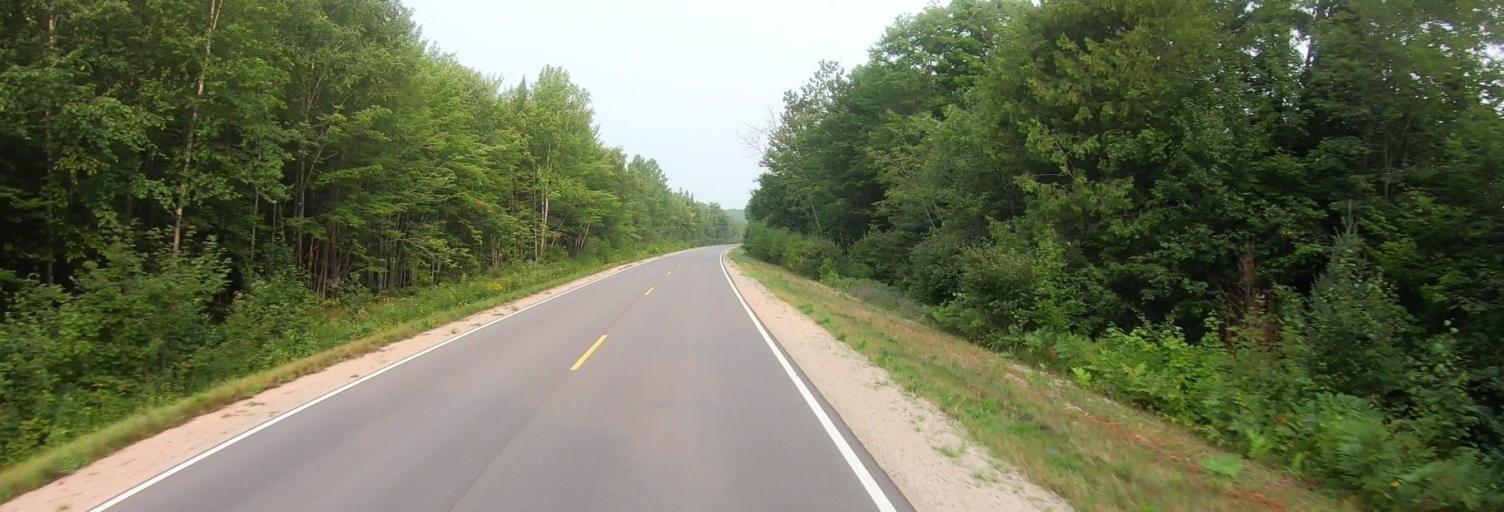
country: US
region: Michigan
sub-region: Luce County
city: Newberry
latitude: 46.4825
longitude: -85.0257
